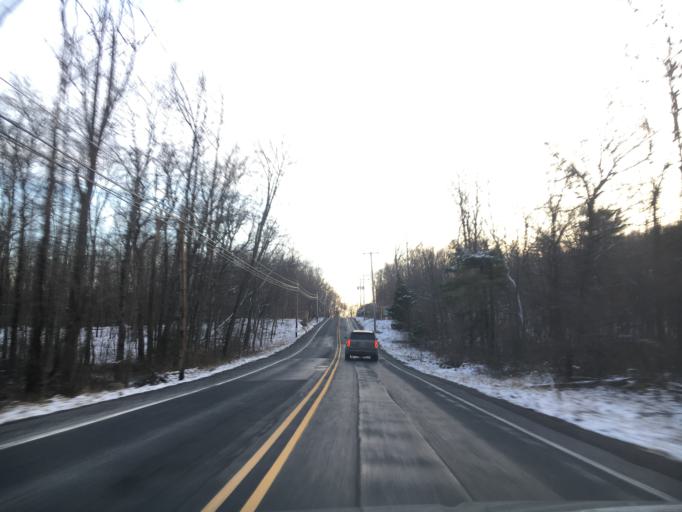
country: US
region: Pennsylvania
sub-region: Pike County
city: Saw Creek
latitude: 41.0983
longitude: -75.0986
